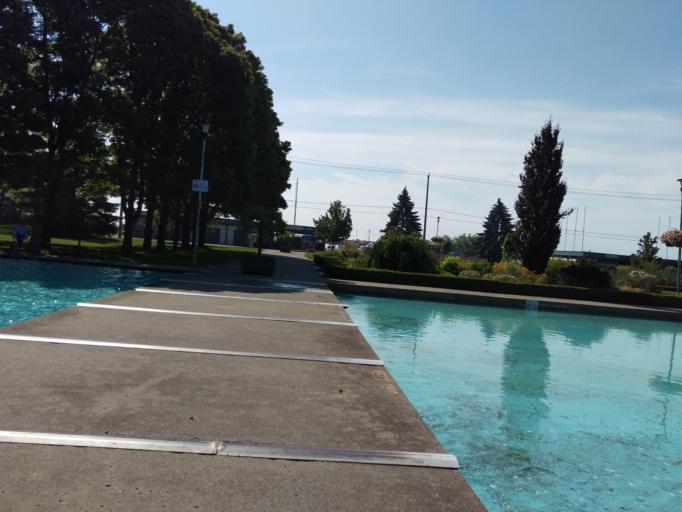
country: CA
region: Ontario
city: Toronto
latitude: 43.6177
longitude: -79.3726
